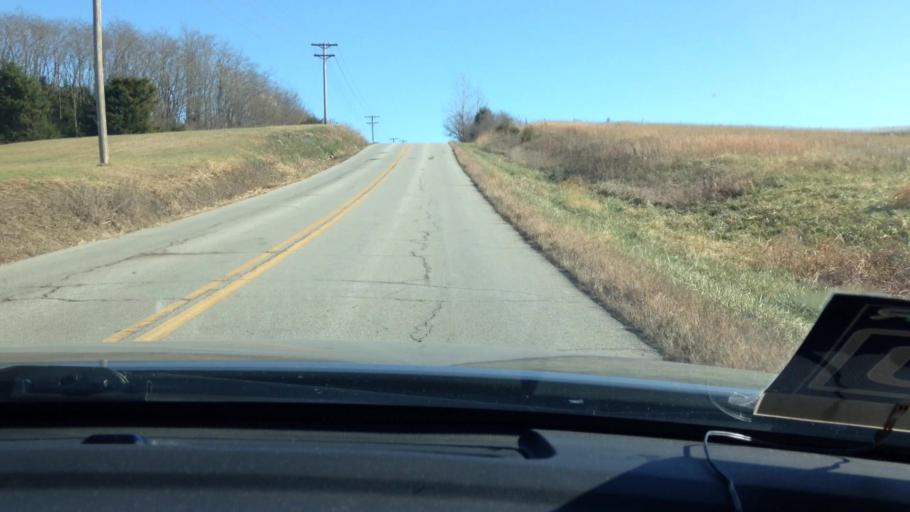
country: US
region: Missouri
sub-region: Platte County
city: Weston
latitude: 39.4828
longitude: -94.8973
